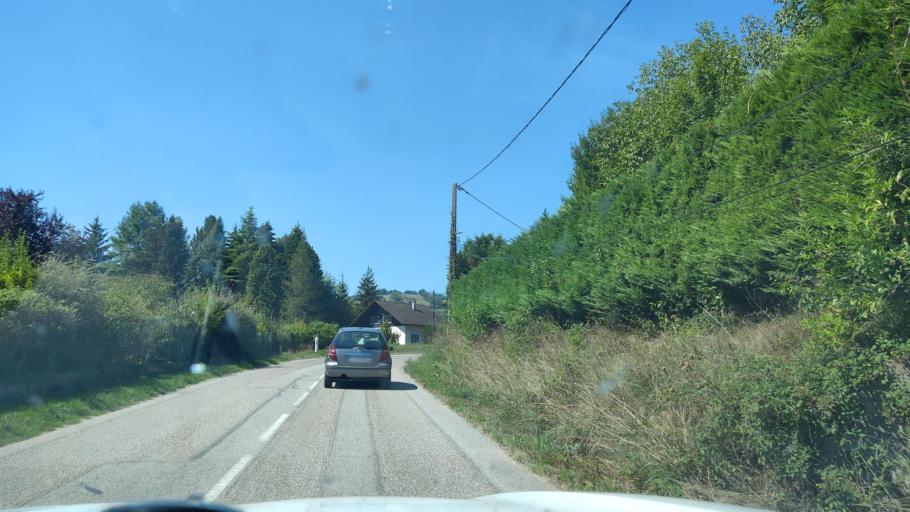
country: FR
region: Rhone-Alpes
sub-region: Departement de la Savoie
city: Novalaise
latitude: 45.6001
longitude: 5.7620
